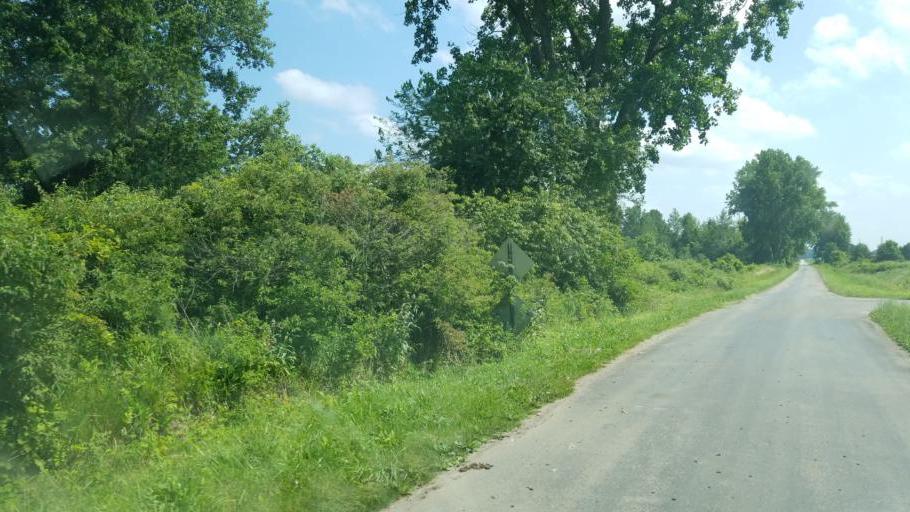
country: US
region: Ohio
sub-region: Huron County
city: Willard
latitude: 41.0105
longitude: -82.7808
